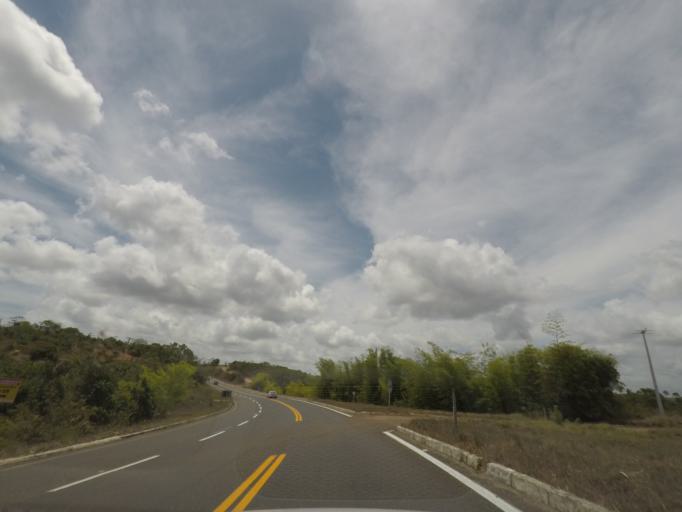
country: BR
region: Sergipe
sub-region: Indiaroba
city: Indiaroba
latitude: -11.5560
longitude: -37.5741
